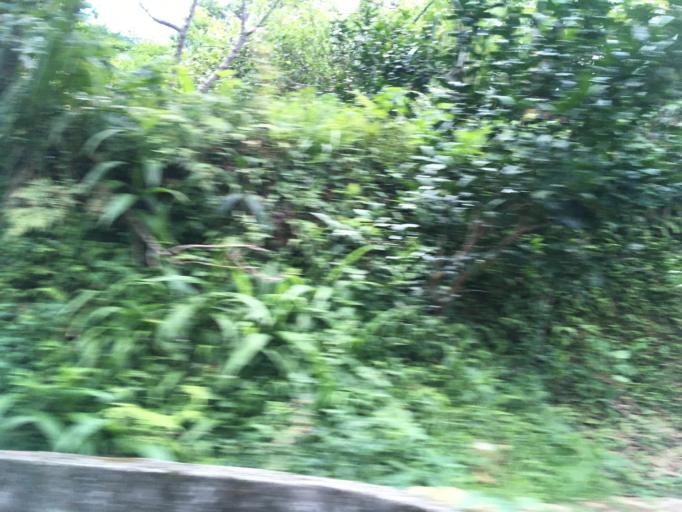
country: TW
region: Taipei
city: Taipei
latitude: 24.9350
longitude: 121.5808
